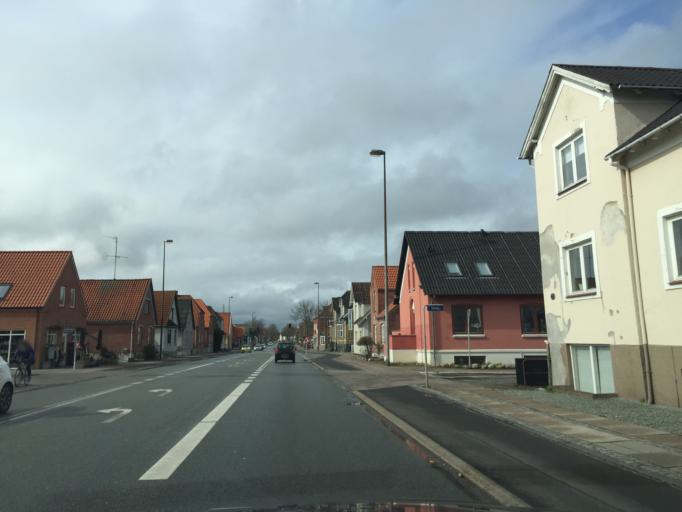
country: DK
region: South Denmark
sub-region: Odense Kommune
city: Odense
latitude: 55.3689
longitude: 10.3721
